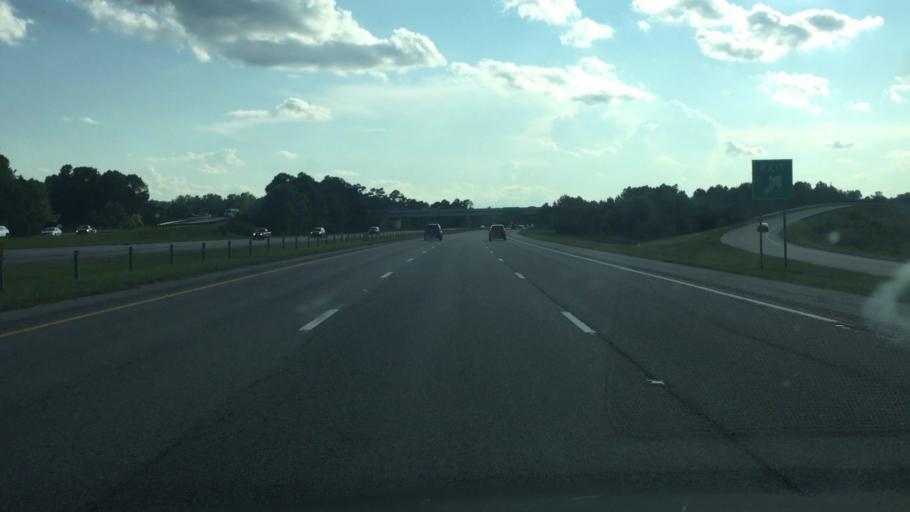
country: US
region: South Carolina
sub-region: Horry County
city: Myrtle Beach
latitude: 33.7555
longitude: -78.8490
